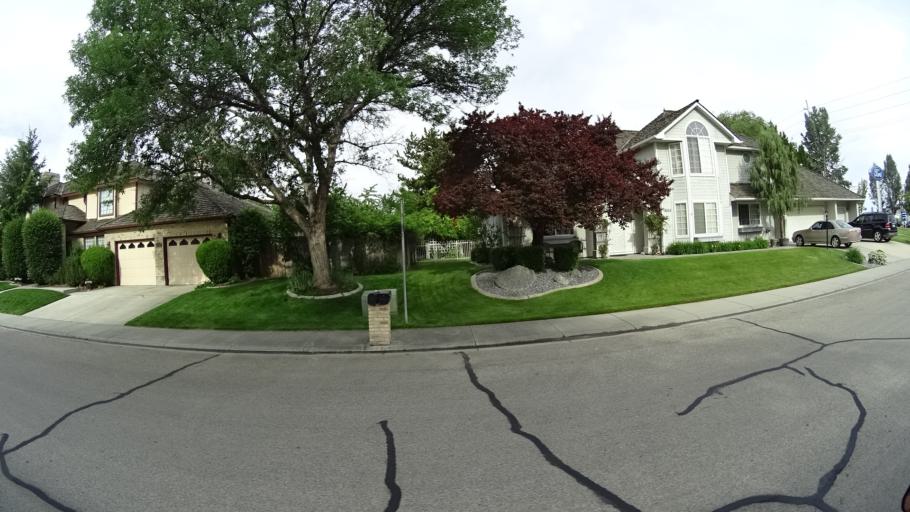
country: US
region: Idaho
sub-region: Ada County
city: Meridian
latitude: 43.5896
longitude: -116.3891
